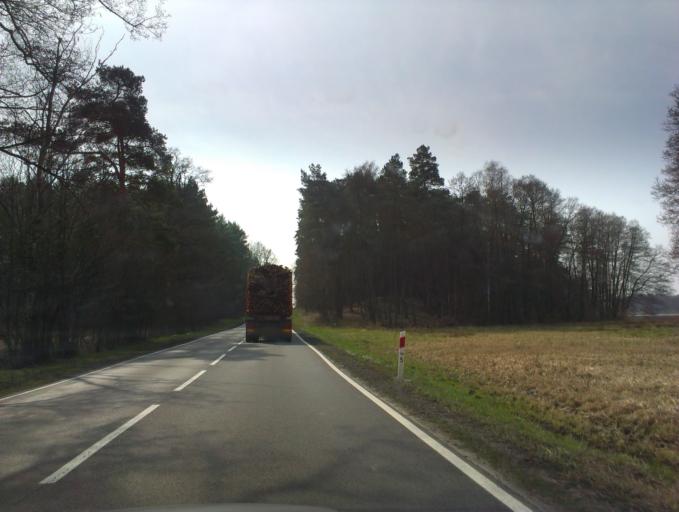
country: PL
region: Greater Poland Voivodeship
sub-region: Powiat pilski
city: Pila
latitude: 53.2283
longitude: 16.7895
